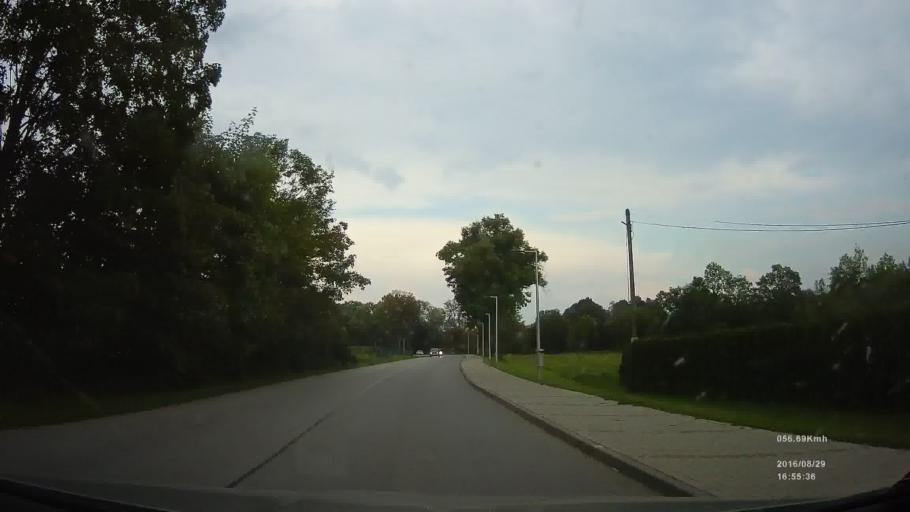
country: SK
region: Zilinsky
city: Ruzomberok
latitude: 49.0979
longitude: 19.4281
